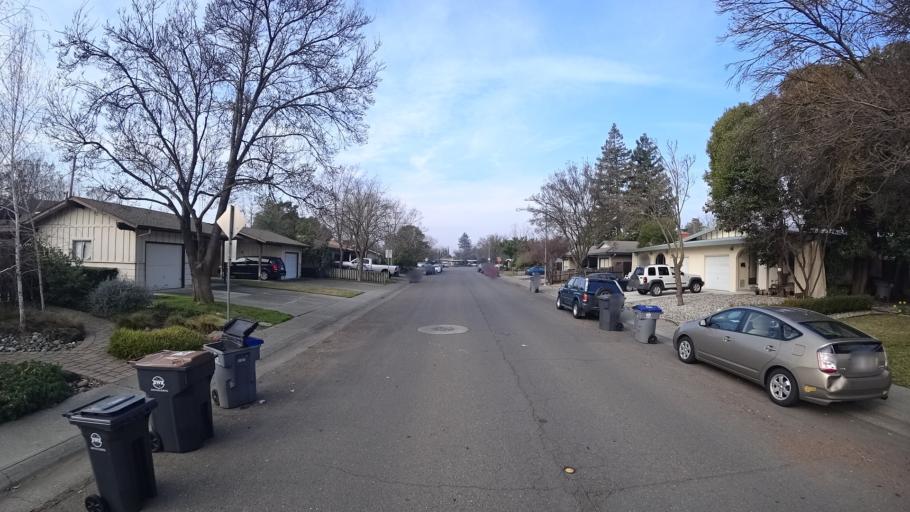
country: US
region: California
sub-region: Yolo County
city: Davis
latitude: 38.5580
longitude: -121.7576
